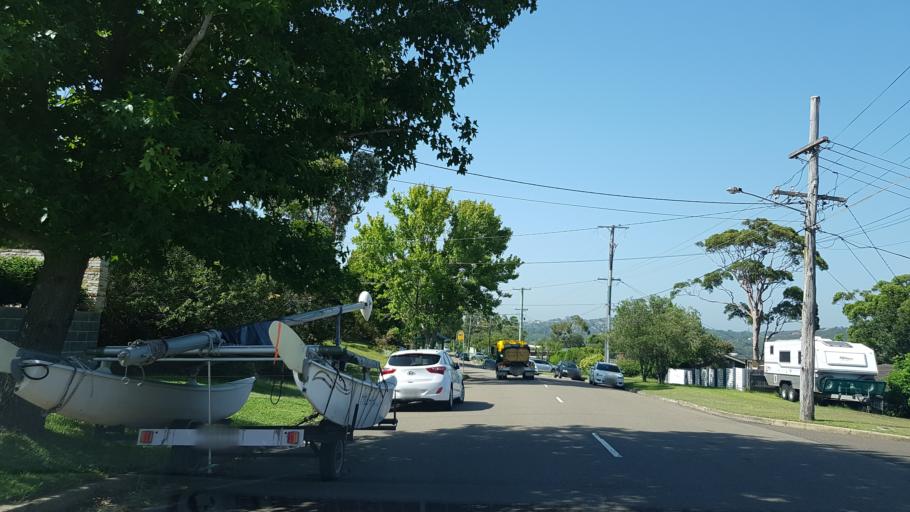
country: AU
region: New South Wales
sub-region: Warringah
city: Narrabeen
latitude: -33.7273
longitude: 151.2801
